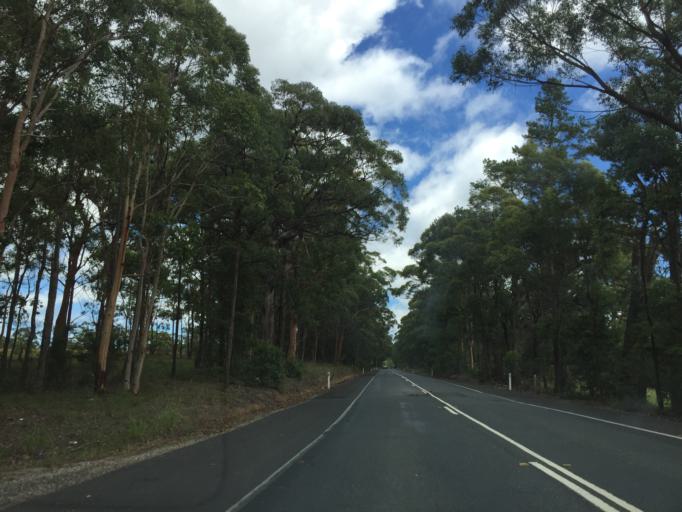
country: AU
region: New South Wales
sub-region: Hawkesbury
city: Richmond
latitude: -33.5073
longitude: 150.5549
